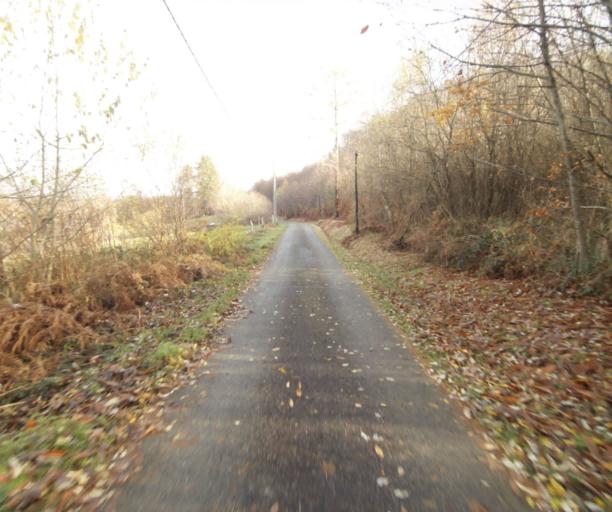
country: FR
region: Limousin
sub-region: Departement de la Correze
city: Sainte-Fortunade
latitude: 45.1977
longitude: 1.7562
